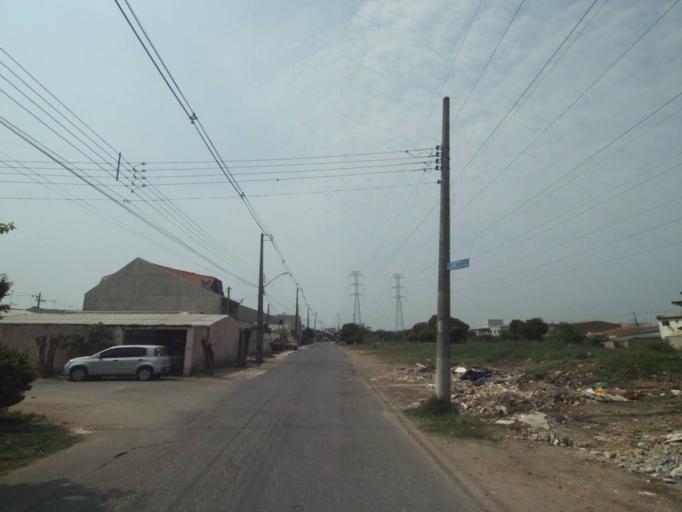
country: BR
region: Parana
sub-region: Pinhais
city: Pinhais
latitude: -25.4852
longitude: -49.1985
